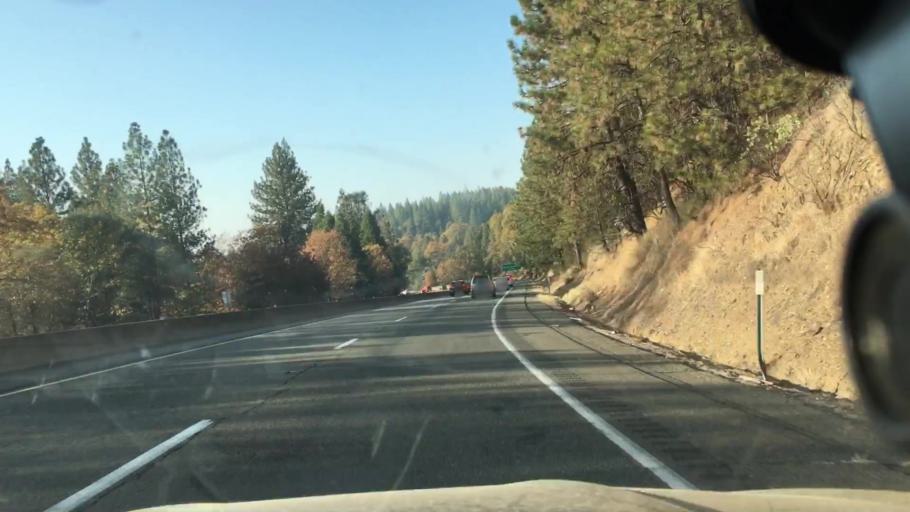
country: US
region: California
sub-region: El Dorado County
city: Placerville
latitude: 38.7314
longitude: -120.7684
